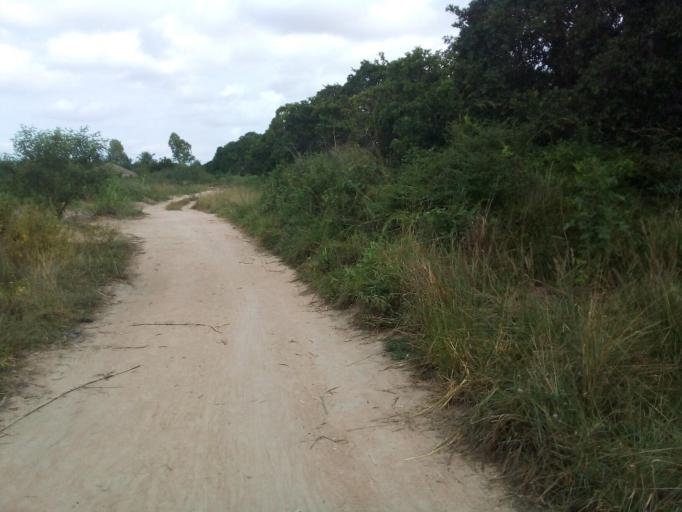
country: MZ
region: Zambezia
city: Quelimane
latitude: -17.5522
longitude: 36.7036
